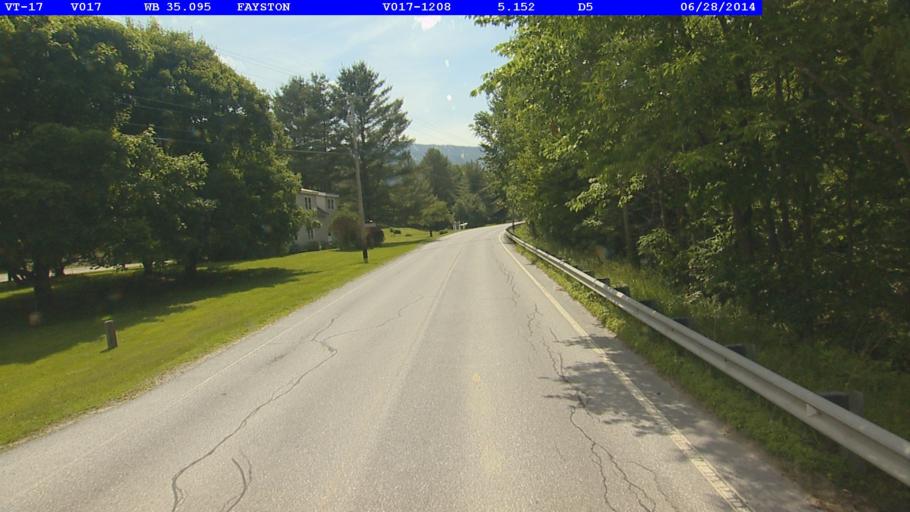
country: US
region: Vermont
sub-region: Washington County
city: Waterbury
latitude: 44.1828
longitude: -72.8560
